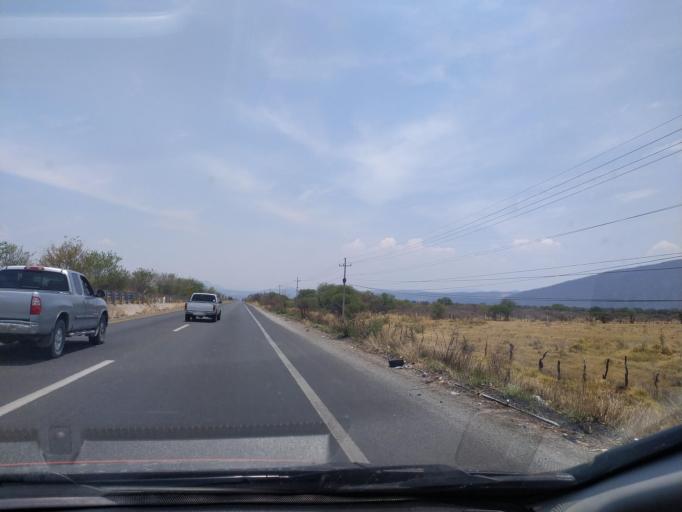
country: MX
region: Jalisco
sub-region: Acatlan de Juarez
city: Villa de los Ninos
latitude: 20.3562
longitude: -103.5917
